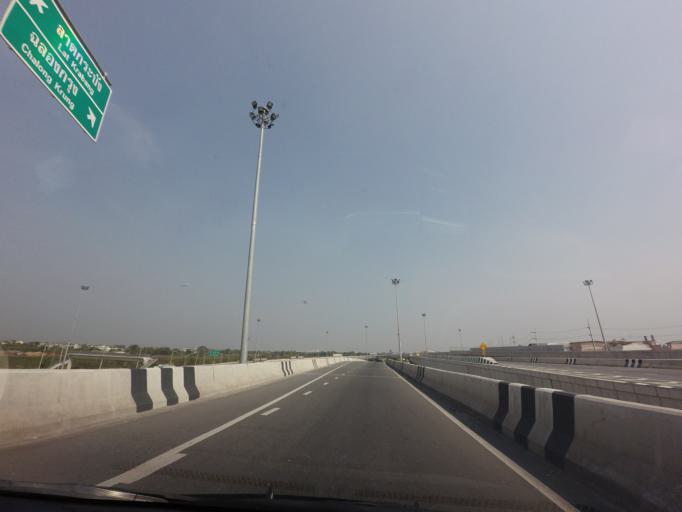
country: TH
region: Bangkok
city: Lat Krabang
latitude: 13.7562
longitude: 100.7460
